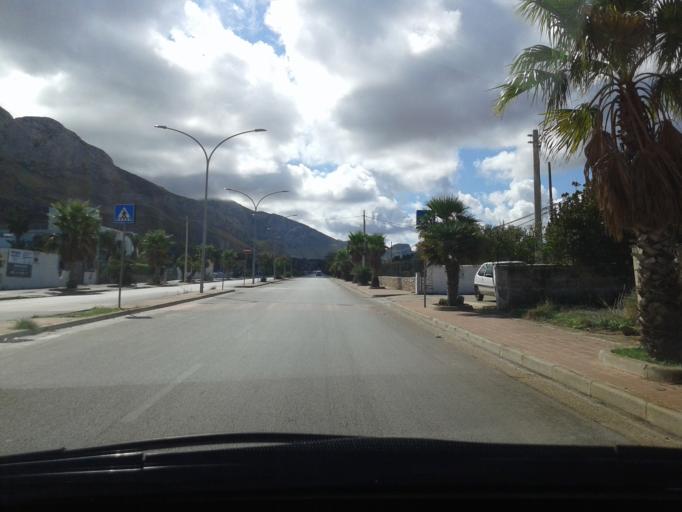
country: IT
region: Sicily
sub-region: Trapani
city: San Vito Lo Capo
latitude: 38.1654
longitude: 12.7355
